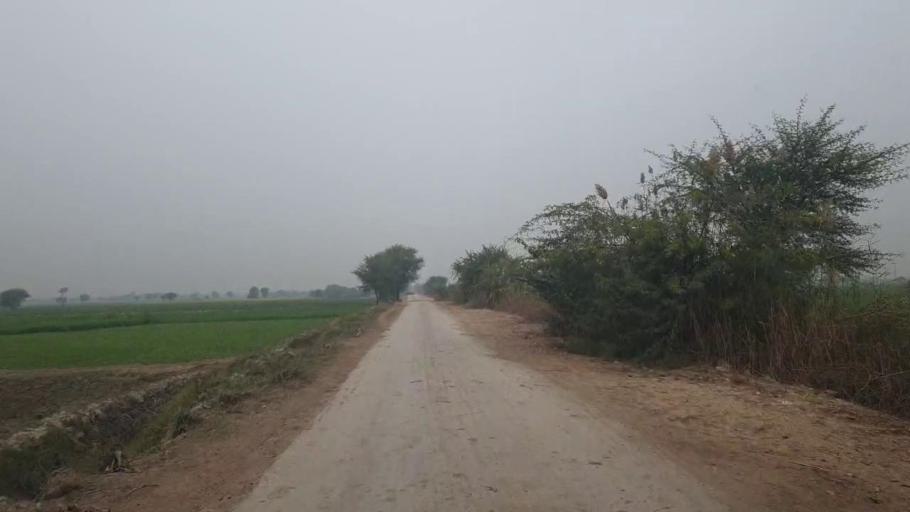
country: PK
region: Sindh
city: Tando Adam
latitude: 25.7727
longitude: 68.6985
